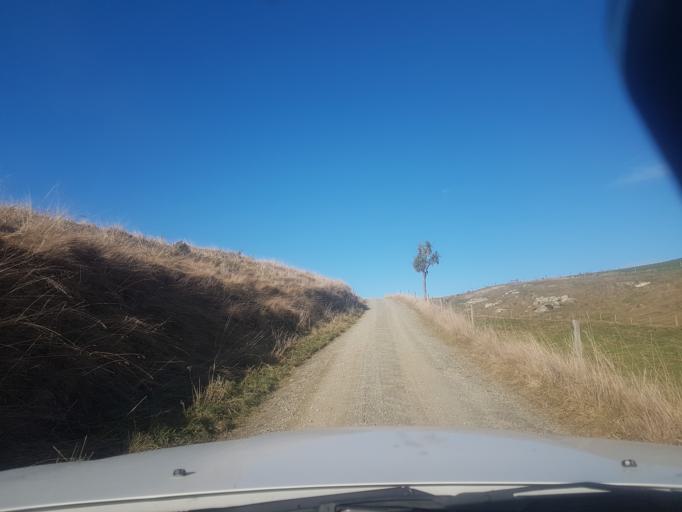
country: NZ
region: Canterbury
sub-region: Timaru District
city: Pleasant Point
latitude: -44.1765
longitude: 170.8888
